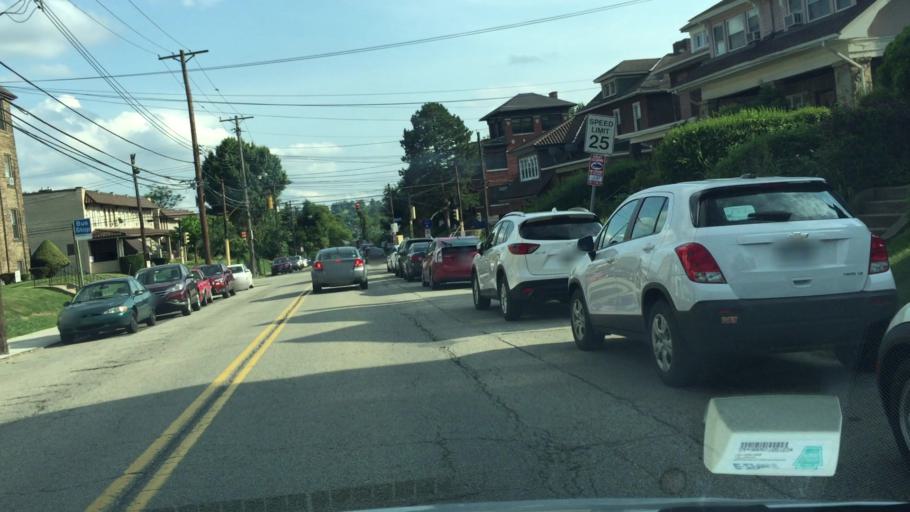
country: US
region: Pennsylvania
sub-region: Allegheny County
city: Homestead
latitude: 40.4316
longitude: -79.9276
